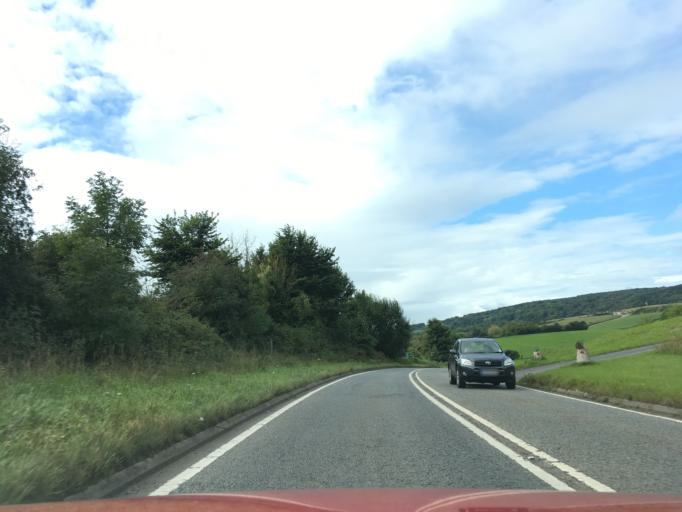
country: GB
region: England
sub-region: Gloucestershire
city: Bream
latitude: 51.6879
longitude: -2.5994
